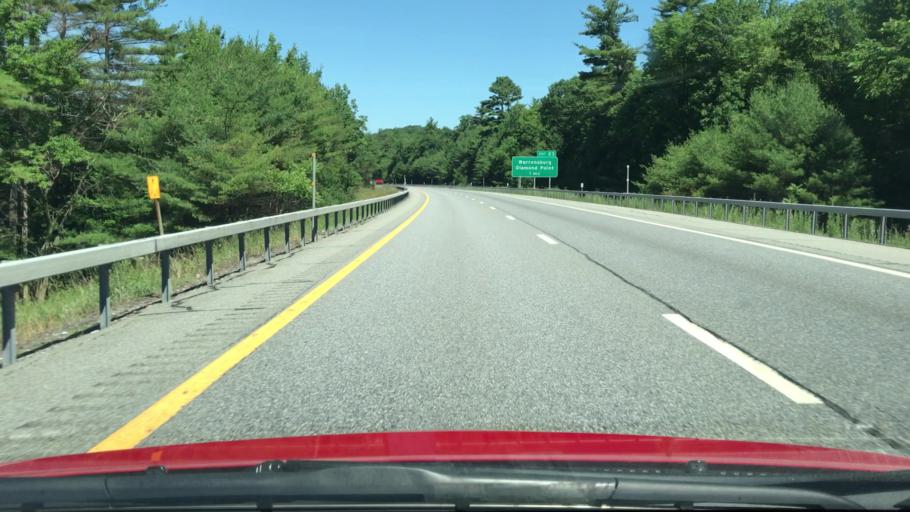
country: US
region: New York
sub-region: Warren County
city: Warrensburg
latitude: 43.4706
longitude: -73.7470
